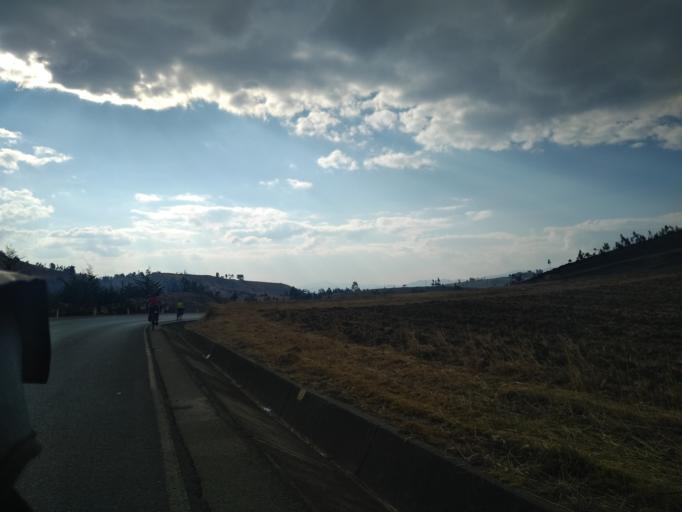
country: PE
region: Cajamarca
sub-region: Provincia de Cajamarca
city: Llacanora
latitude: -7.1469
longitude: -78.3983
